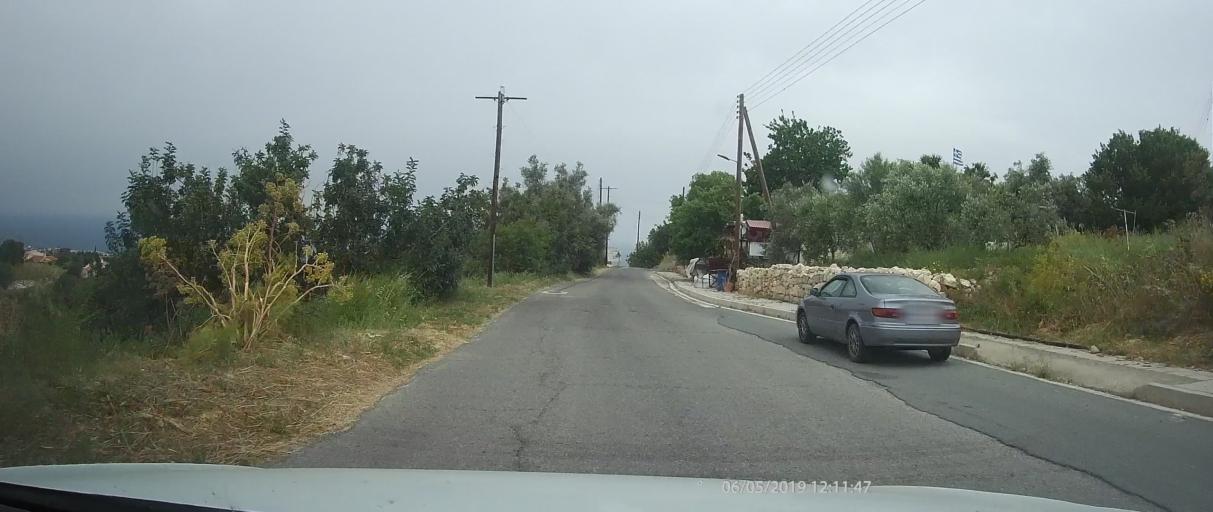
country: CY
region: Pafos
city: Tala
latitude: 34.8390
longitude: 32.4300
